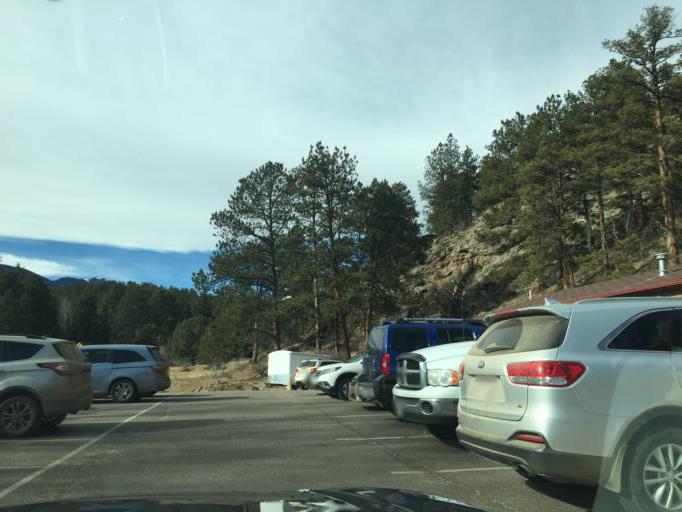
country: US
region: Colorado
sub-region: Jefferson County
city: Evergreen
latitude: 39.4074
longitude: -105.4897
